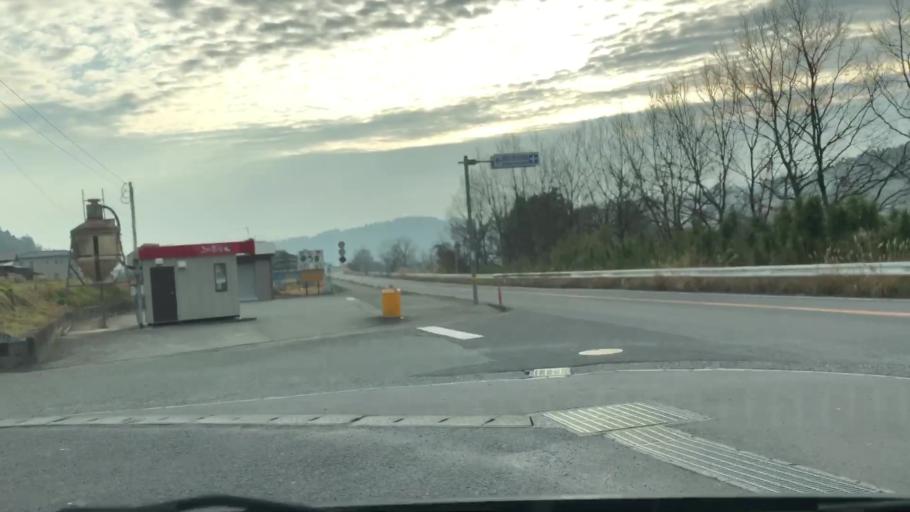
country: JP
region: Oita
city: Takedamachi
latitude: 32.9689
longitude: 131.4749
